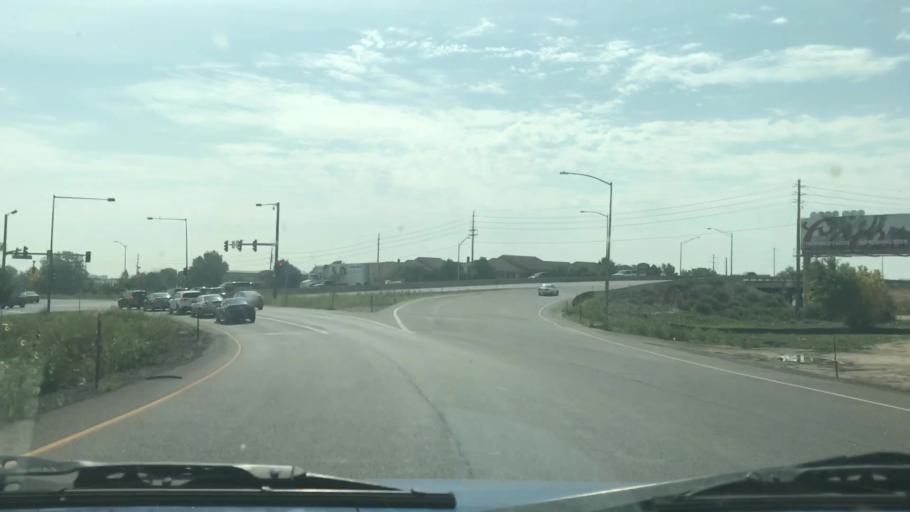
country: US
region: Colorado
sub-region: Adams County
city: Commerce City
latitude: 39.7777
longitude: -104.9046
